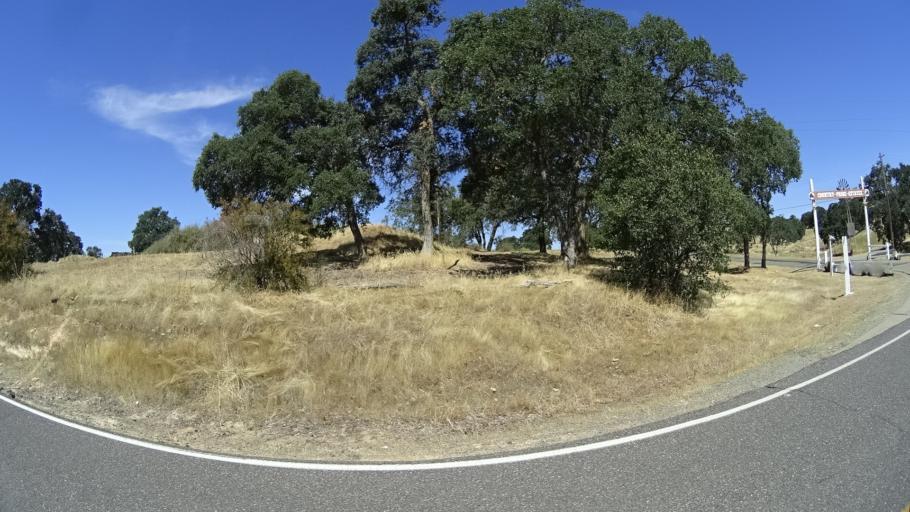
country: US
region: California
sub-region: Calaveras County
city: Rancho Calaveras
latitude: 38.1262
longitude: -120.9086
